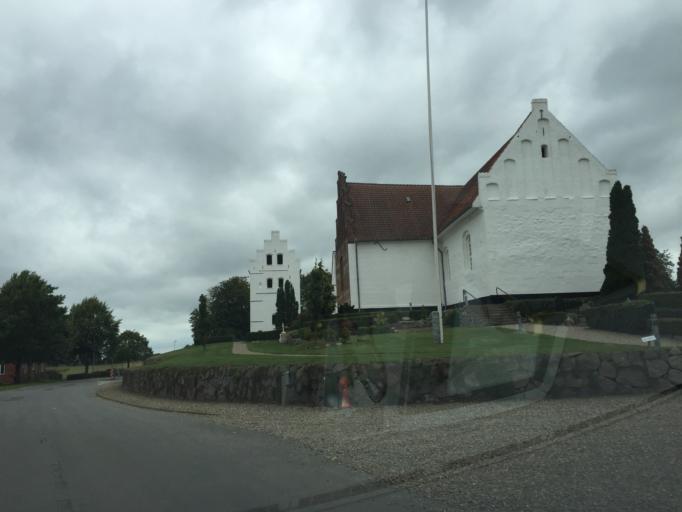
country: DK
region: South Denmark
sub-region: Assens Kommune
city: Arup
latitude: 55.3634
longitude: 9.9894
